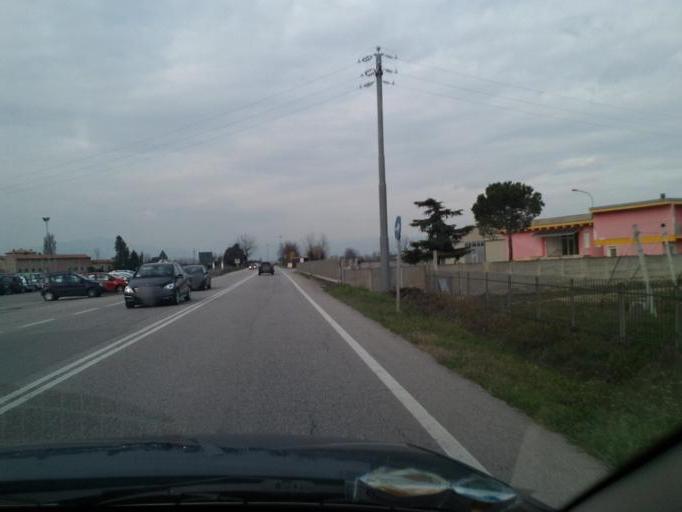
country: IT
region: Veneto
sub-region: Provincia di Verona
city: Sona
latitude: 45.4336
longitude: 10.8481
